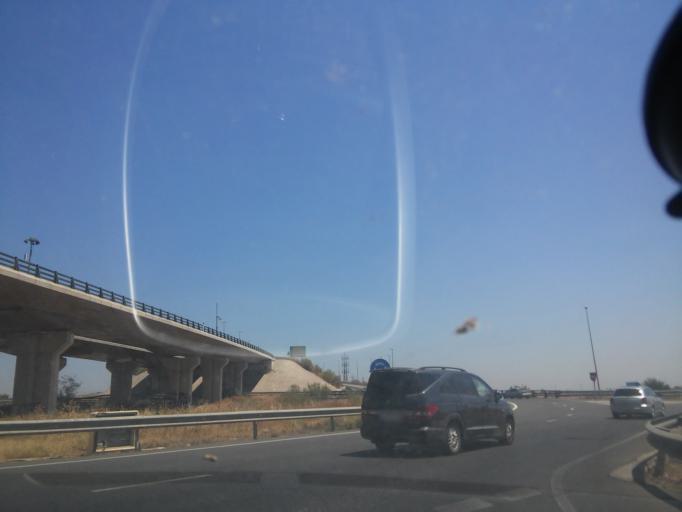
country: ES
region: Andalusia
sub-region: Provincia de Sevilla
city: La Algaba
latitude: 37.4354
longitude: -5.9731
